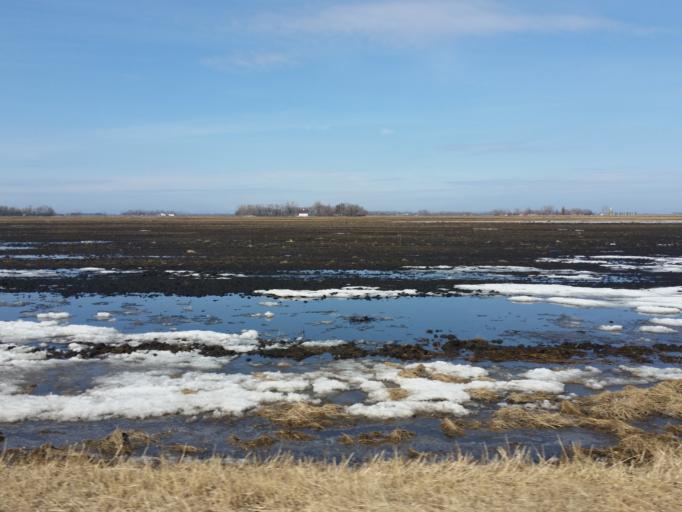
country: US
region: North Dakota
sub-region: Walsh County
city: Grafton
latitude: 48.4413
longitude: -97.4087
